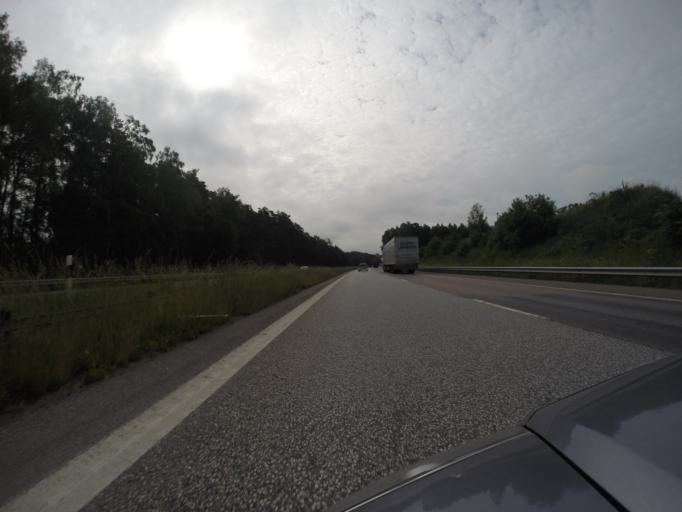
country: SE
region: Skane
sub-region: Landskrona
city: Asmundtorp
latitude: 55.8384
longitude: 12.9217
